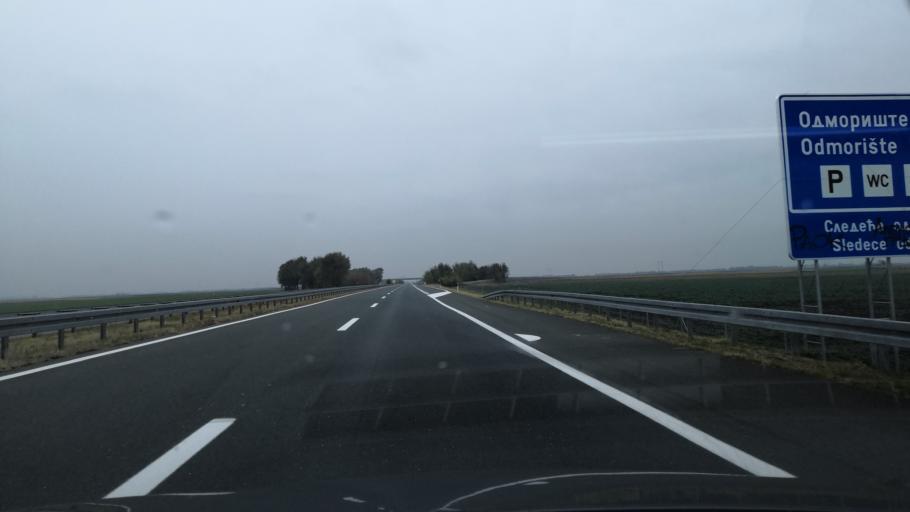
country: RS
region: Autonomna Pokrajina Vojvodina
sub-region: Severnobacki Okrug
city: Subotica
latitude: 45.9936
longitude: 19.7188
